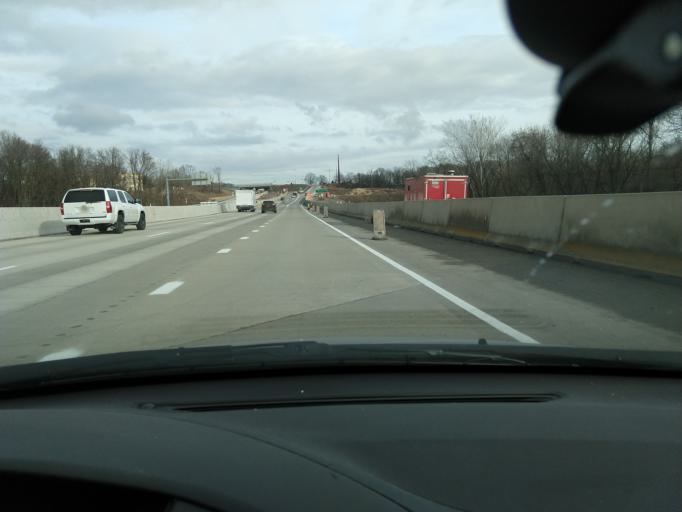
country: US
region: Pennsylvania
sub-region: Chester County
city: Kenilworth
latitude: 40.2320
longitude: -75.6231
